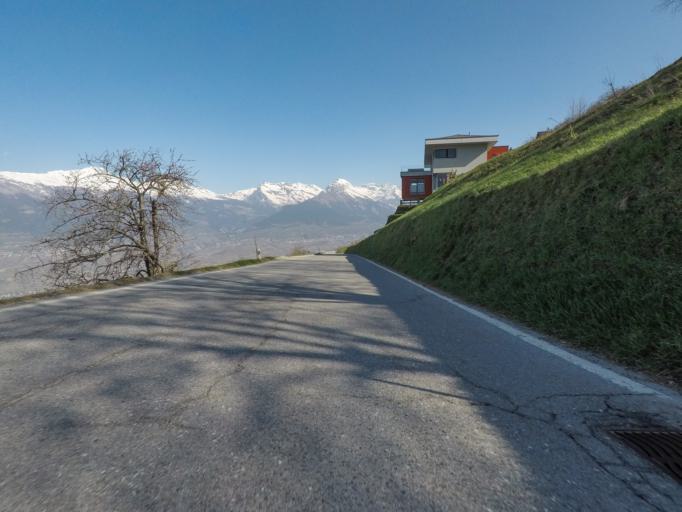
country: CH
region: Valais
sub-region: Conthey District
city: Basse-Nendaz
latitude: 46.1954
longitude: 7.3332
